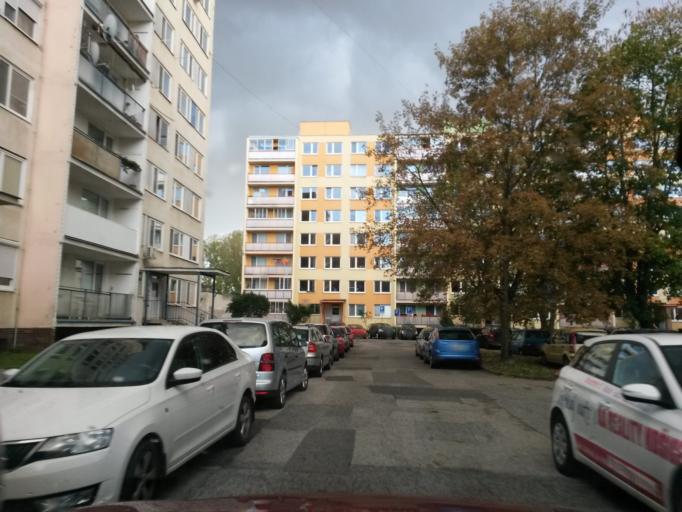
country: SK
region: Kosicky
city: Kosice
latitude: 48.6812
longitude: 21.2981
